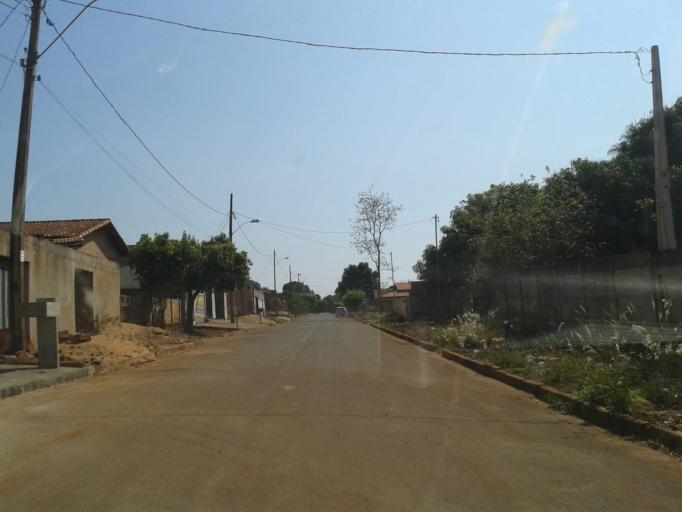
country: BR
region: Minas Gerais
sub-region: Ituiutaba
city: Ituiutaba
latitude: -18.9619
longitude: -49.4832
